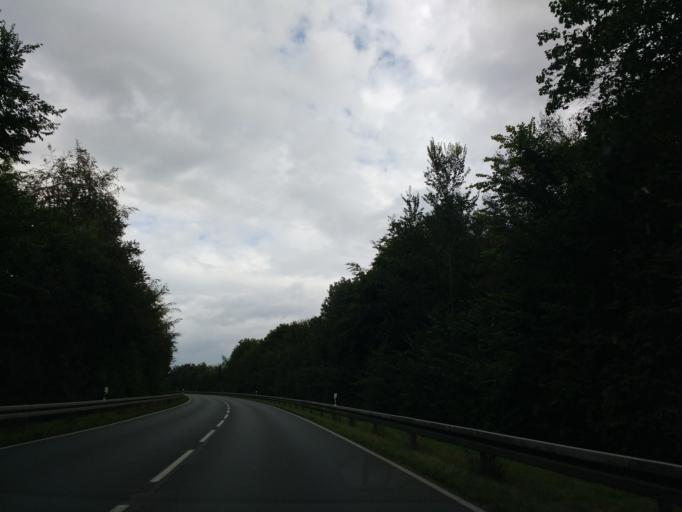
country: DE
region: Lower Saxony
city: Bad Rothenfelde
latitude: 52.1010
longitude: 8.1612
